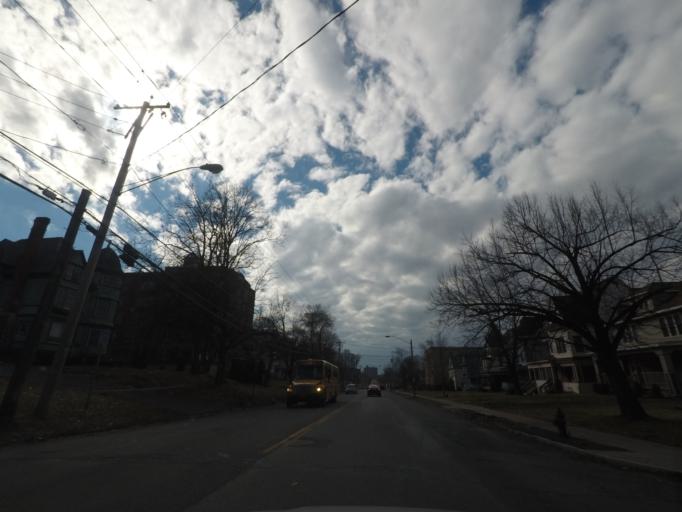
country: US
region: New York
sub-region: Onondaga County
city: Syracuse
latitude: 43.0471
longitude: -76.1258
